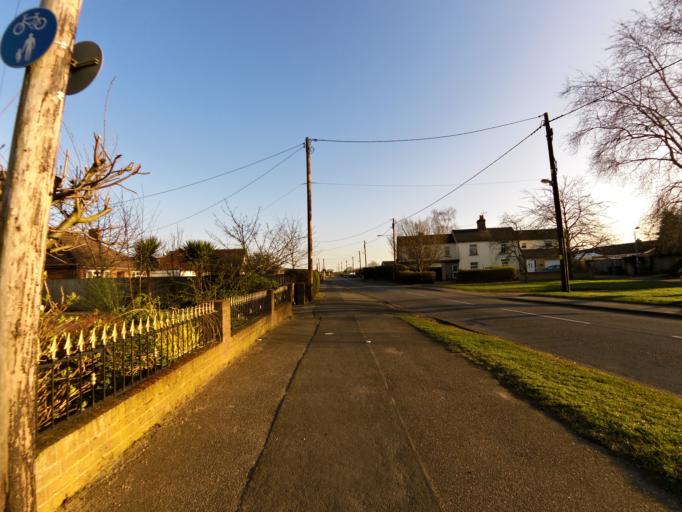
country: GB
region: England
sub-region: Suffolk
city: Kesgrave
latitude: 52.0605
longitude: 1.2333
